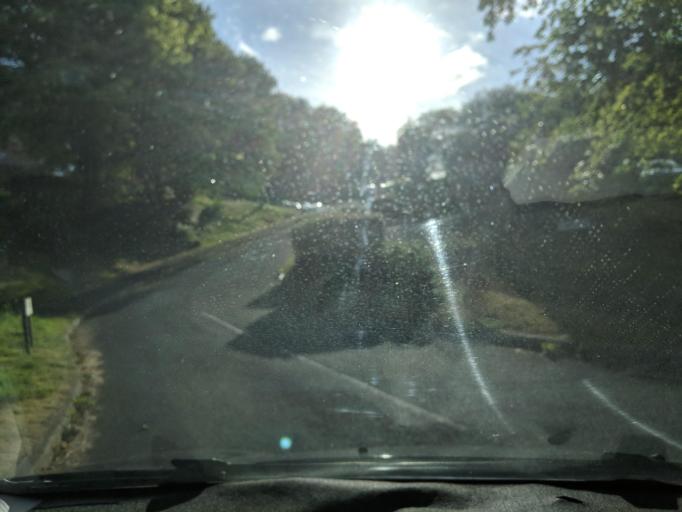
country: GB
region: England
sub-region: Plymouth
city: Plymstock
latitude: 50.3935
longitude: -4.1056
